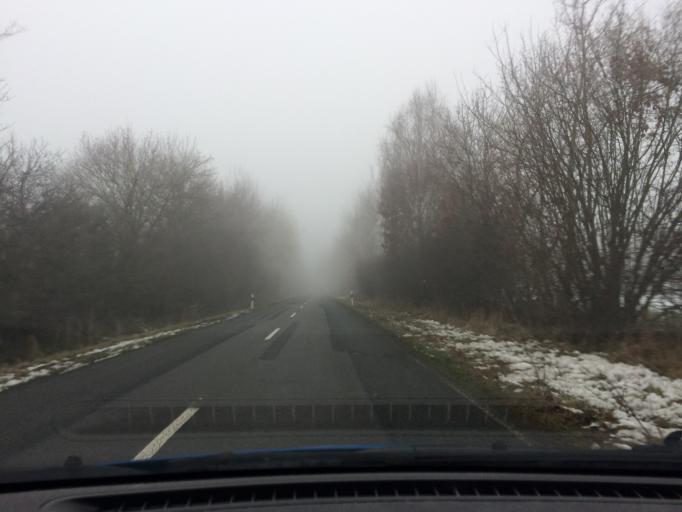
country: DE
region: Schleswig-Holstein
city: Juliusburg
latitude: 53.4081
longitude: 10.5086
